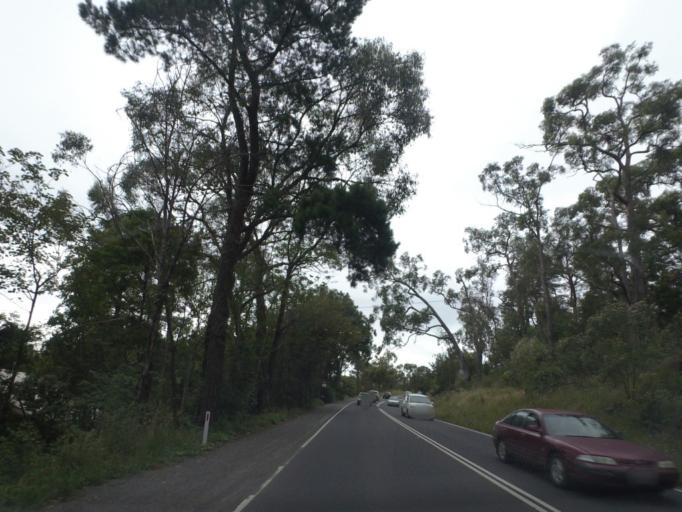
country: AU
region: Victoria
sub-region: Yarra Ranges
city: Mount Evelyn
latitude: -37.7901
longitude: 145.3763
